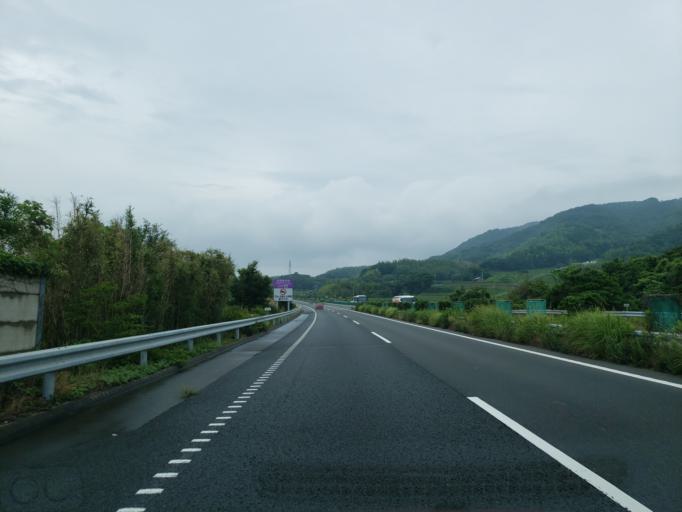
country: JP
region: Hyogo
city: Sumoto
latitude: 34.3908
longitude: 134.8589
